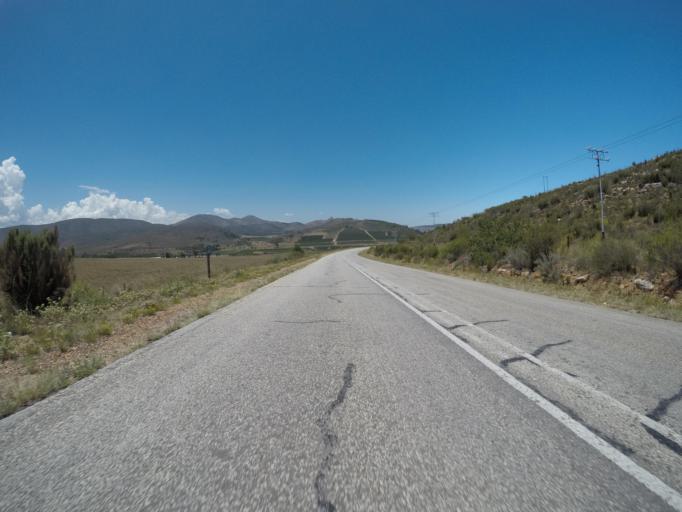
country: ZA
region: Western Cape
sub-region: Eden District Municipality
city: Plettenberg Bay
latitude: -33.7445
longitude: 23.4759
